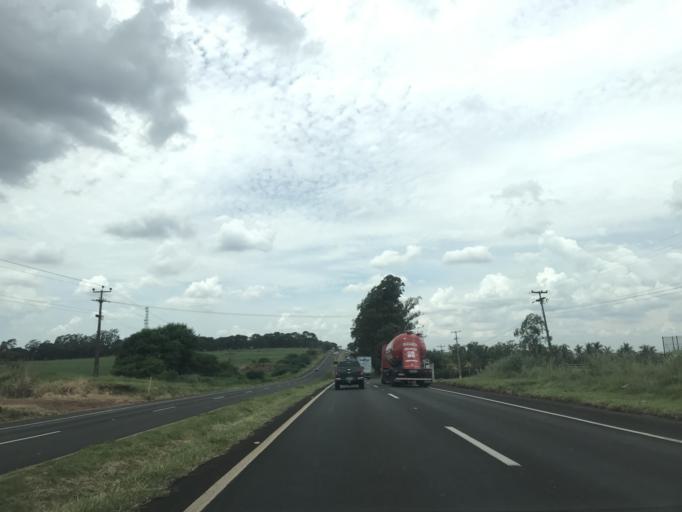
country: BR
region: Parana
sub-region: Paicandu
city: Paicandu
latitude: -23.3864
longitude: -52.0237
